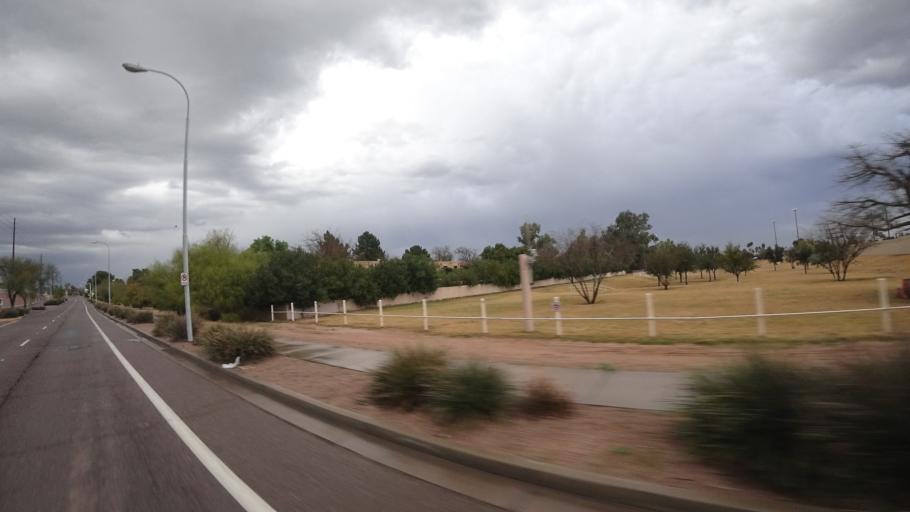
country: US
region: Arizona
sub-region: Maricopa County
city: Paradise Valley
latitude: 33.4850
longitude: -111.9428
